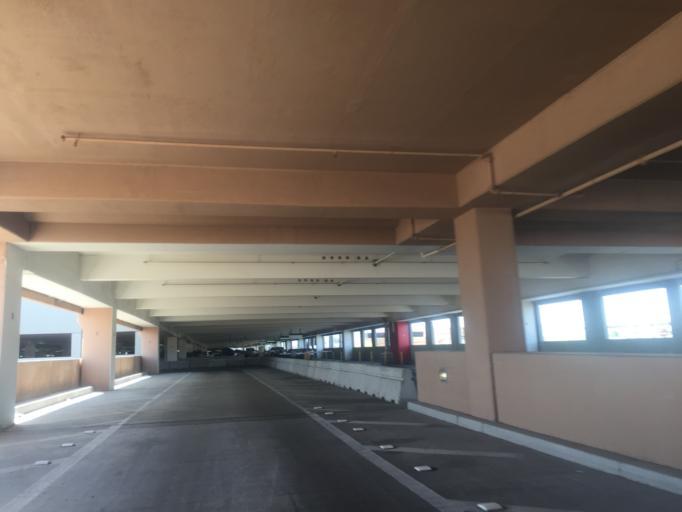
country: US
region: Arizona
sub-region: Maricopa County
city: Phoenix
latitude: 33.4323
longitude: -112.0464
